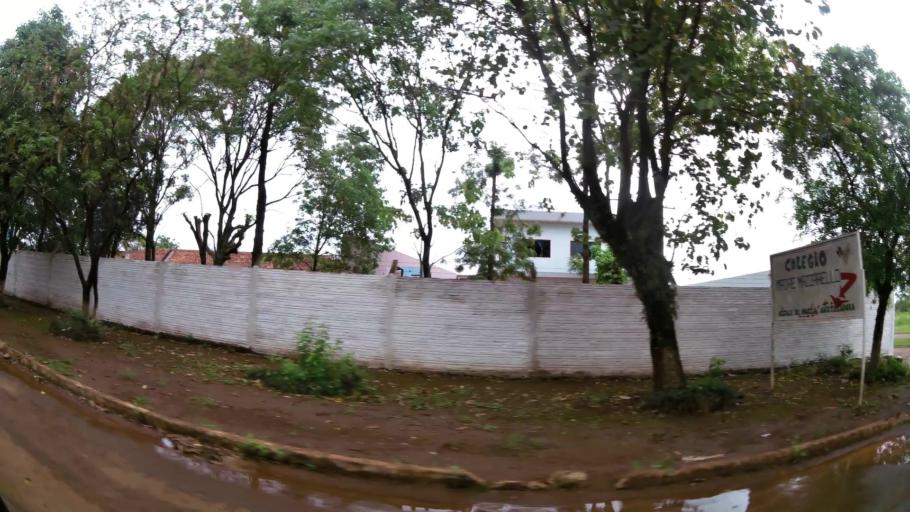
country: PY
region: Alto Parana
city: Ciudad del Este
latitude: -25.4796
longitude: -54.7594
